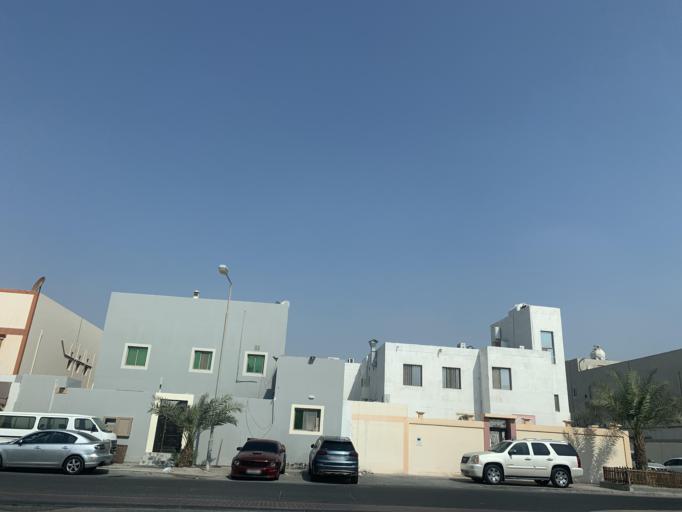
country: BH
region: Central Governorate
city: Madinat Hamad
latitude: 26.1252
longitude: 50.4936
